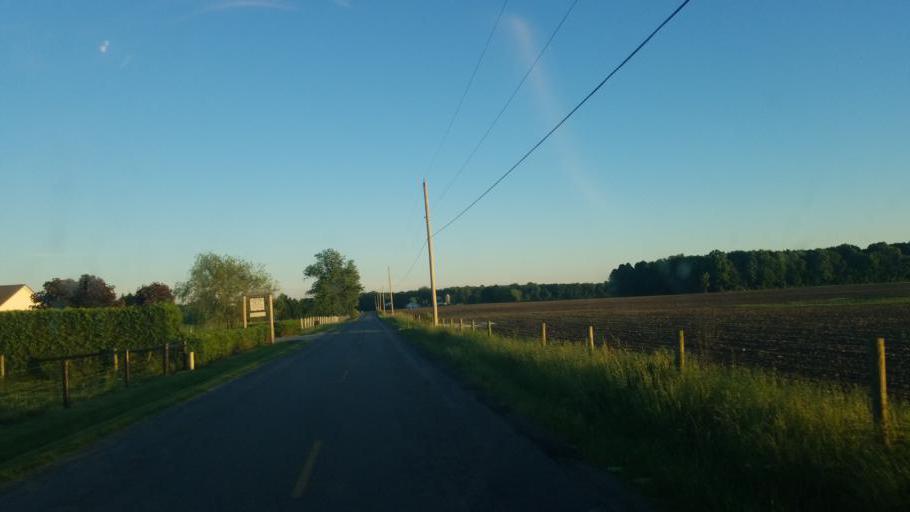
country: US
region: Indiana
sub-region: Elkhart County
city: Nappanee
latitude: 41.4406
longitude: -86.0304
